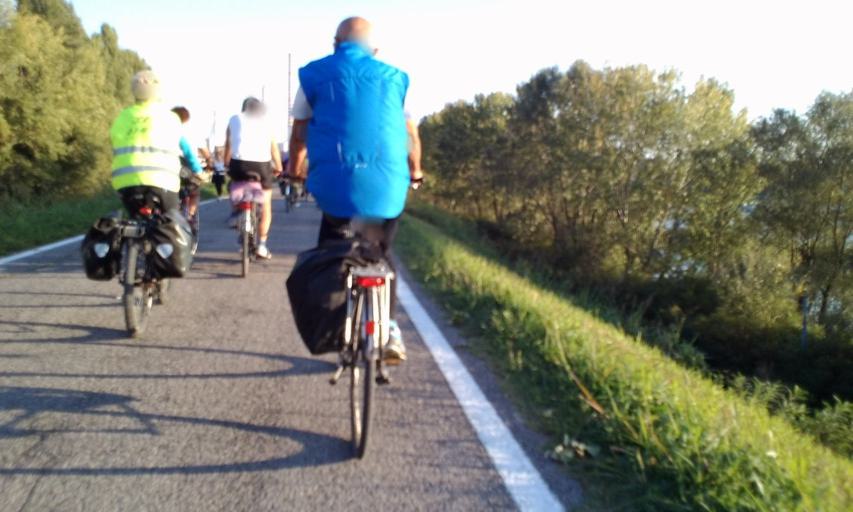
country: IT
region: Lombardy
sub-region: Provincia di Mantova
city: Ostiglia
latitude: 45.0692
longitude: 11.1282
